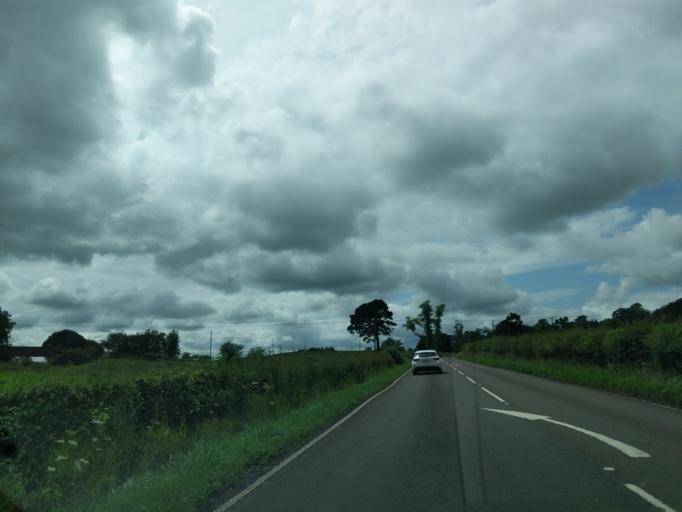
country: GB
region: Scotland
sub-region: South Lanarkshire
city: Strathaven
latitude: 55.6832
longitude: -4.0300
